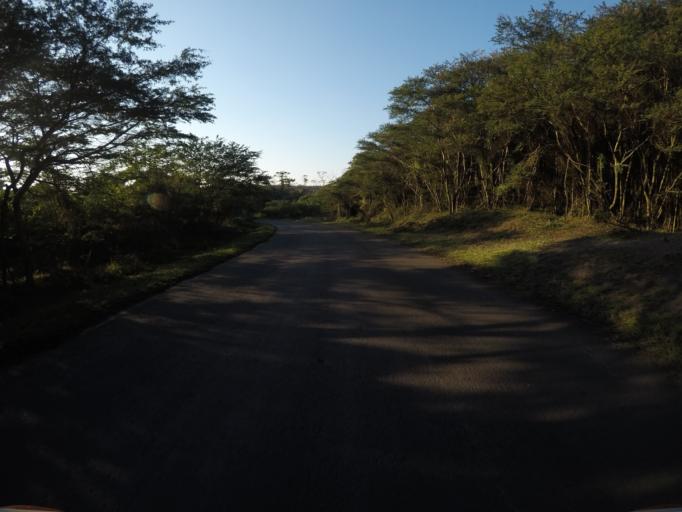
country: ZA
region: KwaZulu-Natal
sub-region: uThungulu District Municipality
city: KwaMbonambi
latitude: -28.6948
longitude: 32.2106
